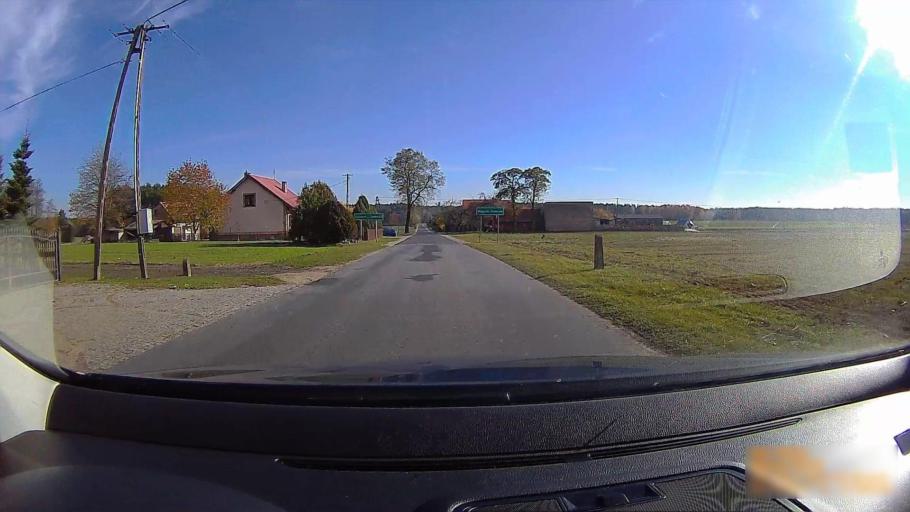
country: PL
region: Greater Poland Voivodeship
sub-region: Powiat ostrzeszowski
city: Ostrzeszow
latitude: 51.4122
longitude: 17.9837
